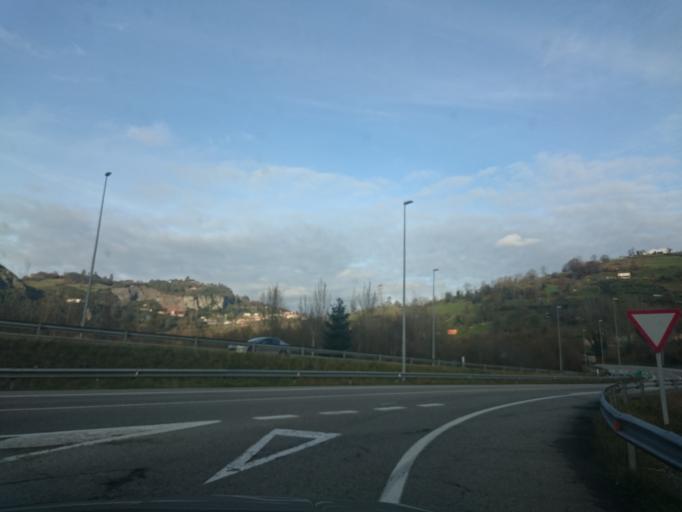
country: ES
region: Asturias
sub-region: Province of Asturias
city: Oviedo
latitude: 43.2987
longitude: -5.8319
